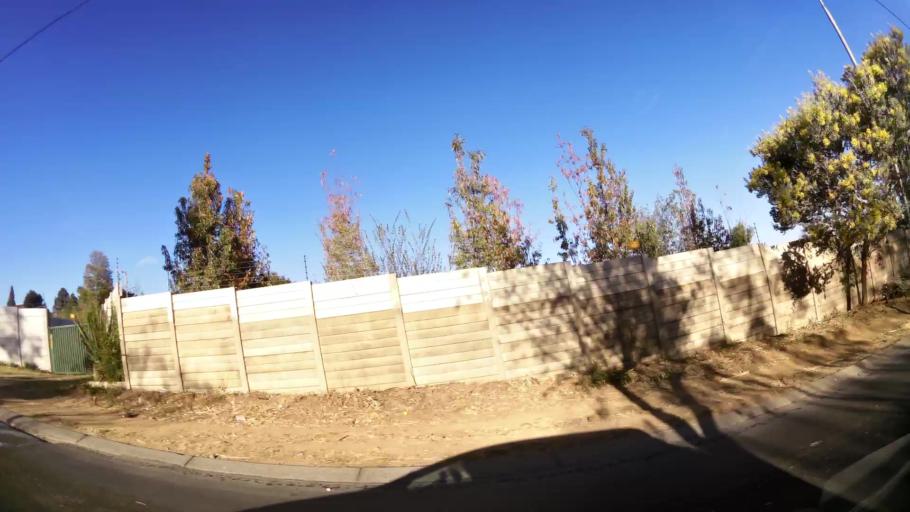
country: ZA
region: Gauteng
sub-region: City of Johannesburg Metropolitan Municipality
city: Midrand
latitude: -26.0200
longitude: 28.1434
